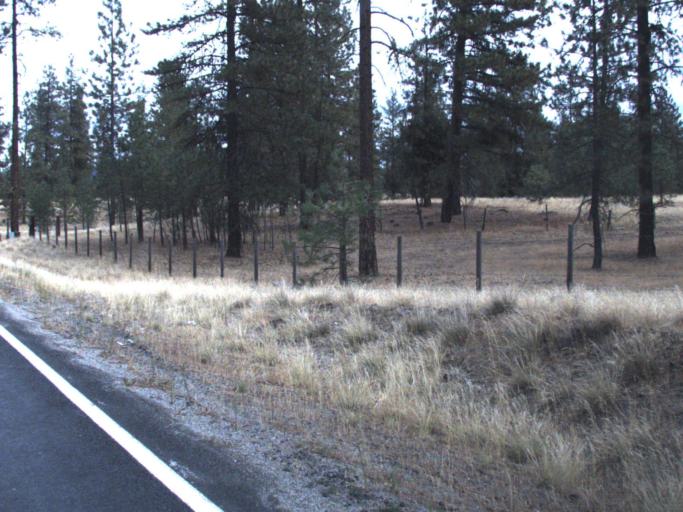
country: US
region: Washington
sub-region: Spokane County
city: Fairchild Air Force Base
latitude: 47.8884
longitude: -117.8325
